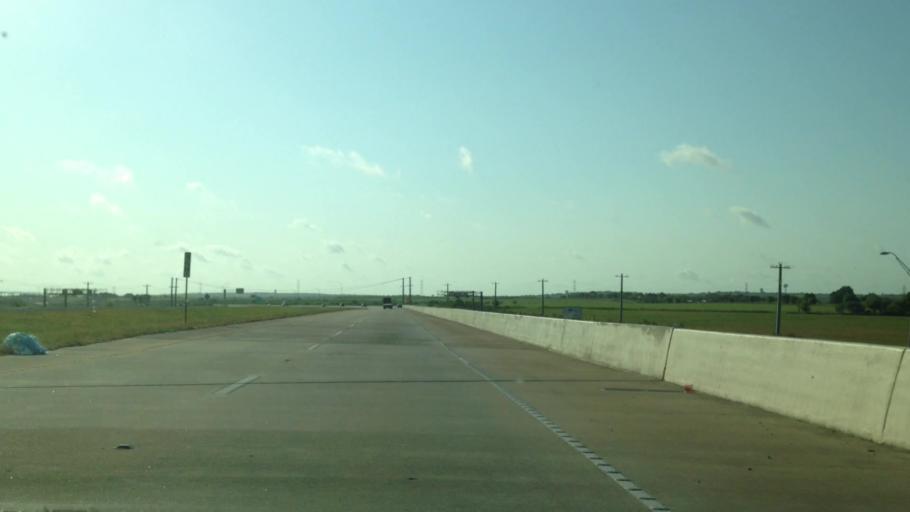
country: US
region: Texas
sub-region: Travis County
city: Onion Creek
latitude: 30.0833
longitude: -97.7351
